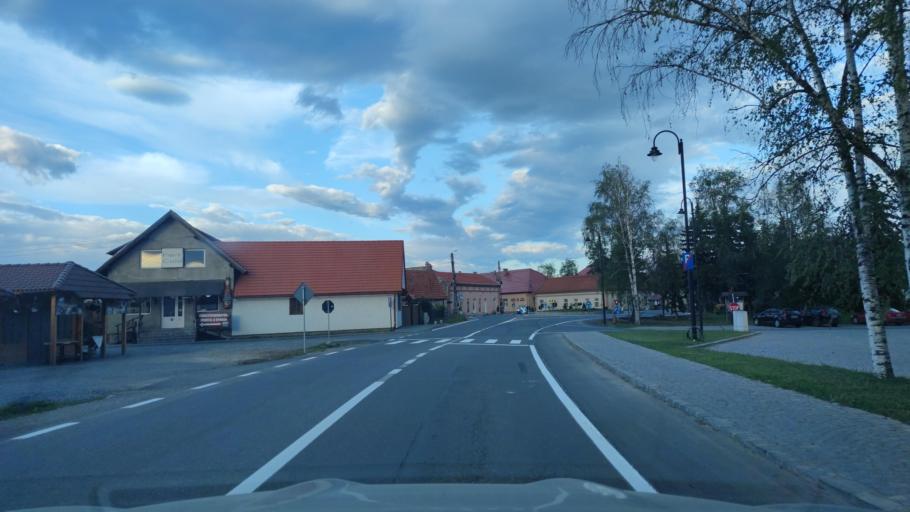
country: RO
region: Harghita
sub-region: Comuna Joseni
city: Joseni
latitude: 46.7020
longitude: 25.5029
